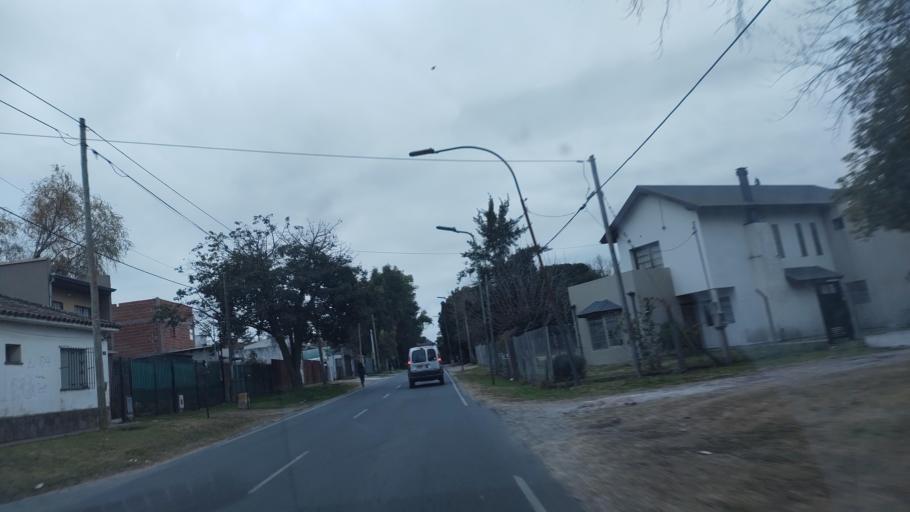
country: AR
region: Buenos Aires
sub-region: Partido de La Plata
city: La Plata
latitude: -34.8577
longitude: -58.0972
